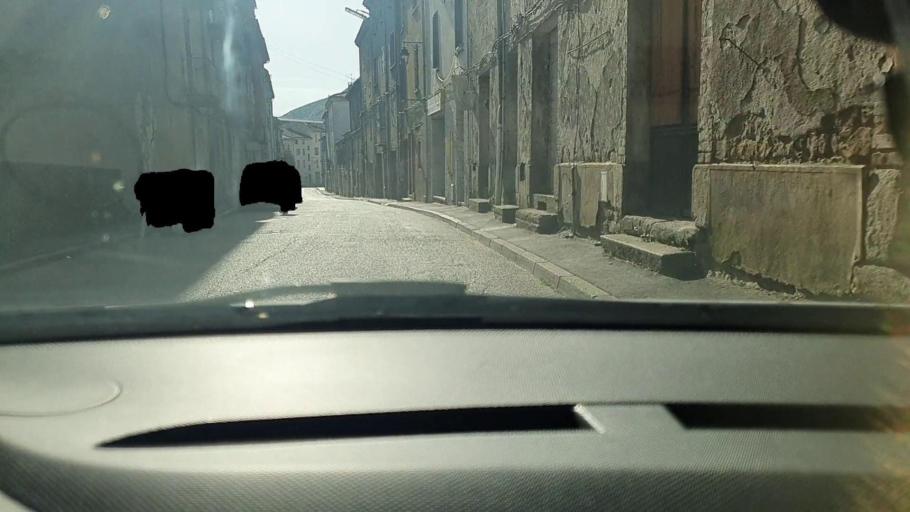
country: FR
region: Languedoc-Roussillon
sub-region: Departement du Gard
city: Besseges
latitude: 44.2966
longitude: 4.0902
